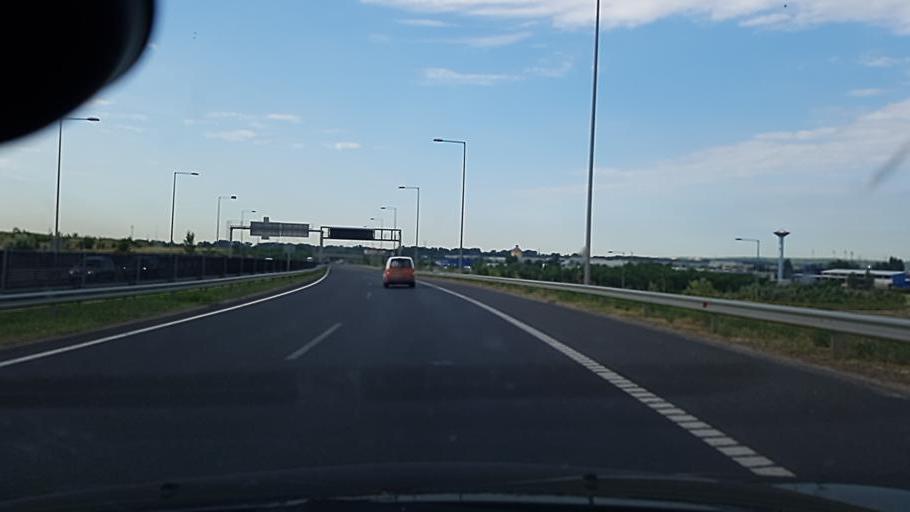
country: HU
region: Pest
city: Diosd
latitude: 47.3968
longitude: 18.9686
